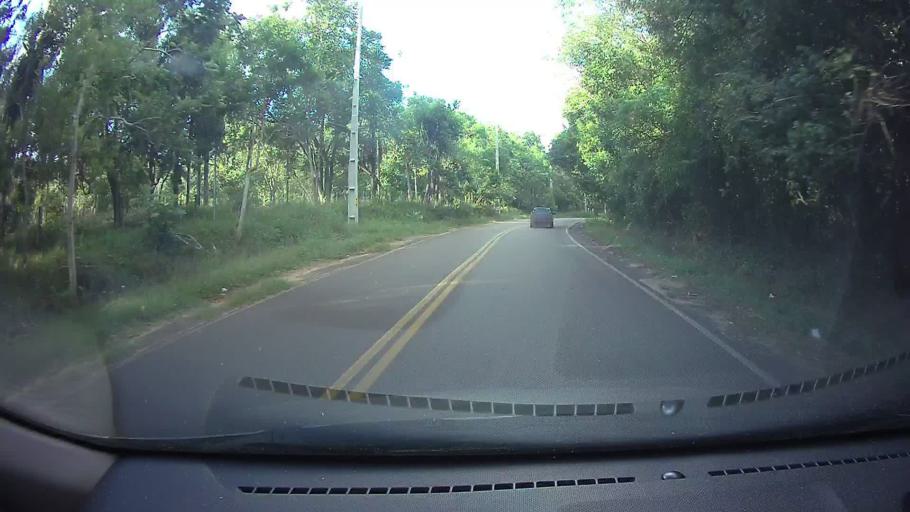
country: PY
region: Cordillera
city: Altos
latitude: -25.2331
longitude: -57.2300
